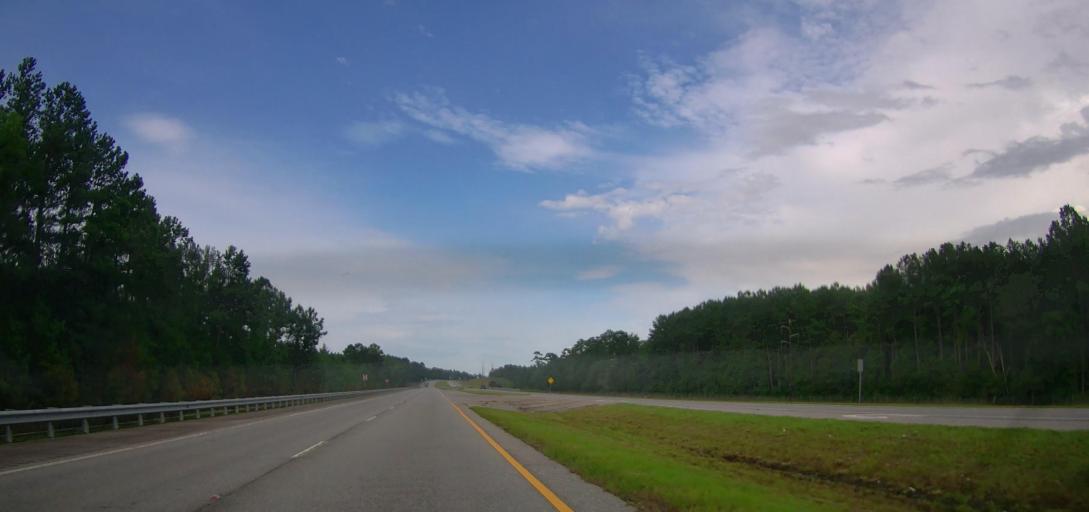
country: US
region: Georgia
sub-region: Wayne County
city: Jesup
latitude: 31.4622
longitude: -82.0507
